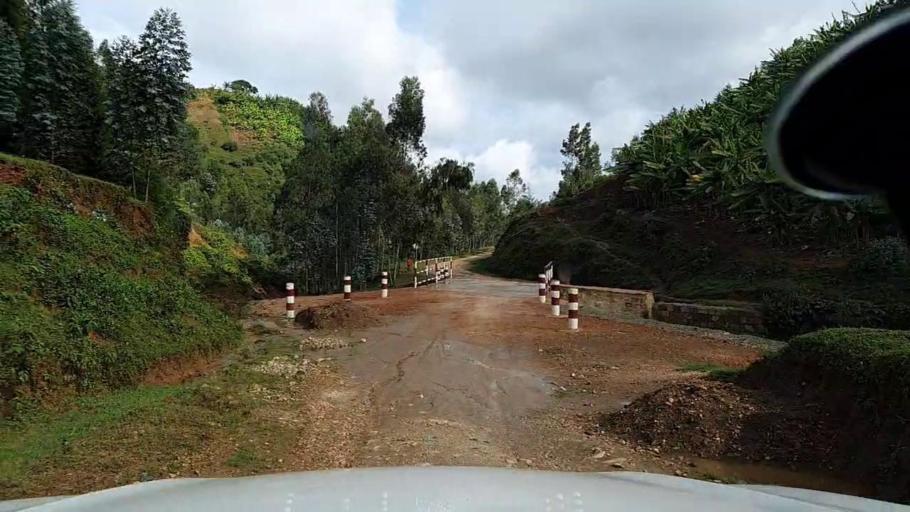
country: RW
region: Western Province
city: Kibuye
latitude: -2.1297
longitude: 29.4988
